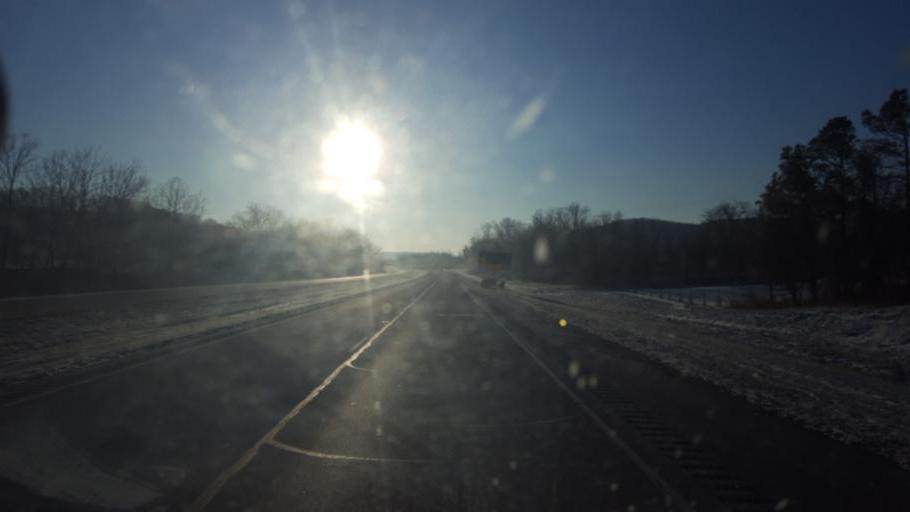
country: US
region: Ohio
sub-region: Pike County
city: Piketon
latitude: 39.0556
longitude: -83.0657
